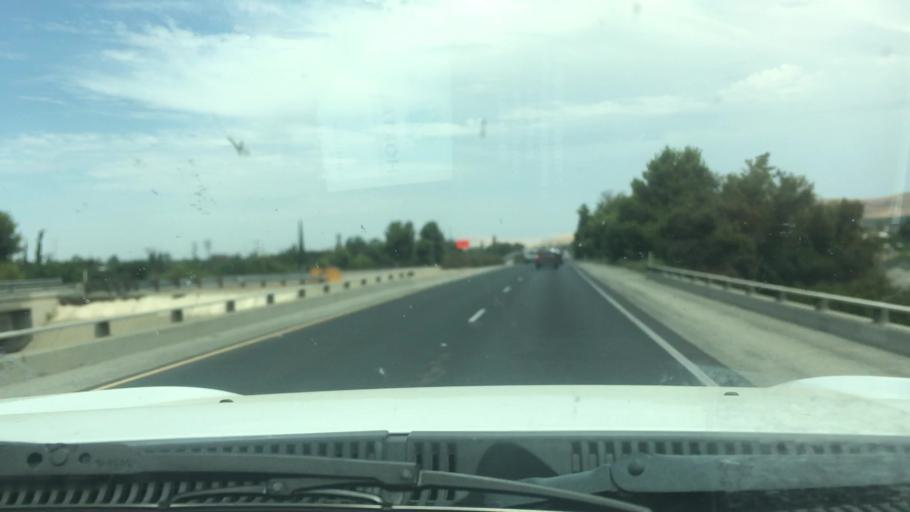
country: US
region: California
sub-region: Tulare County
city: Porterville
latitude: 36.0731
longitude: -119.0395
